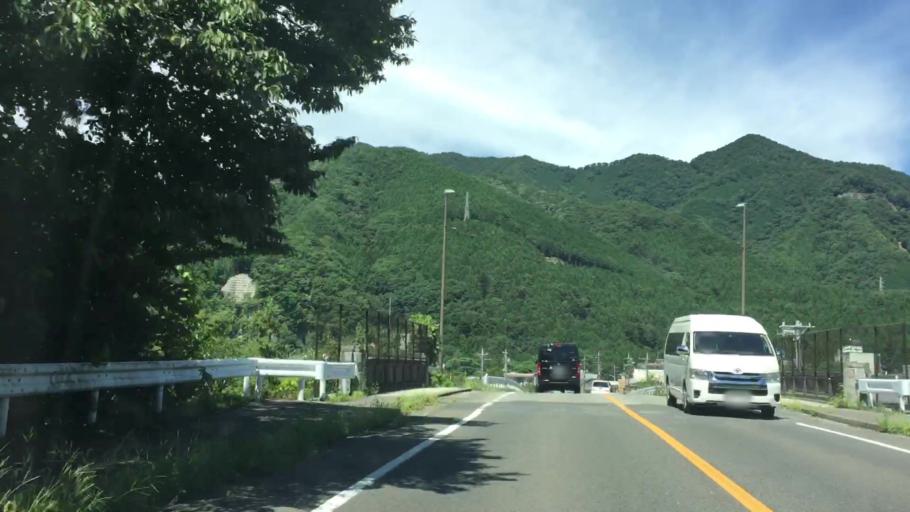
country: JP
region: Tochigi
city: Imaichi
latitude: 36.8199
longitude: 139.7151
